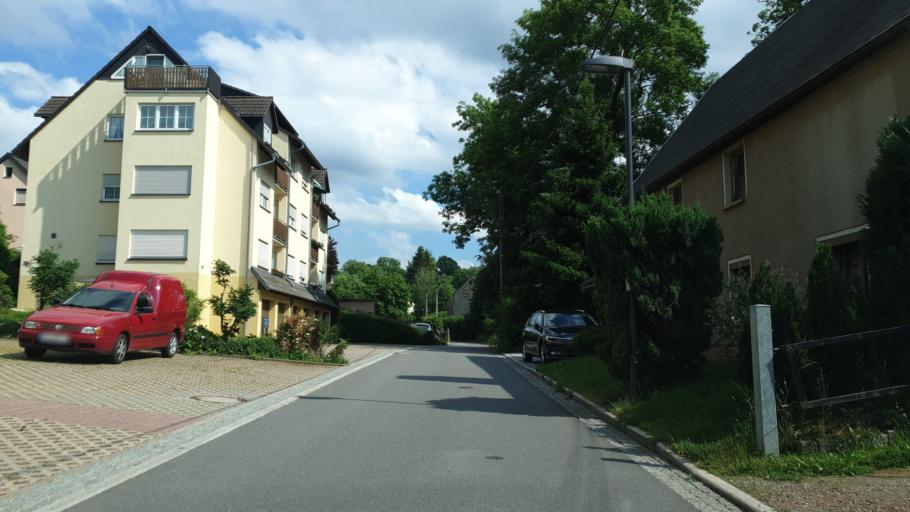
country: DE
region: Saxony
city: Lugau
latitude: 50.7403
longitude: 12.7339
